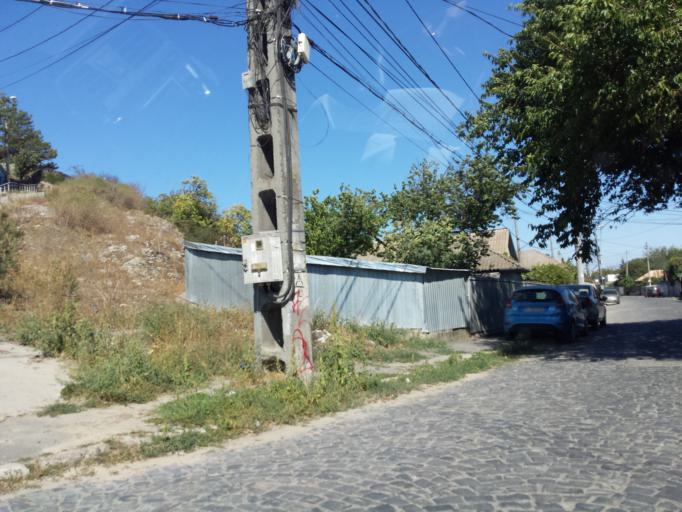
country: RO
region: Tulcea
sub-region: Municipiul Tulcea
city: Tulcea
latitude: 45.1859
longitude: 28.8175
